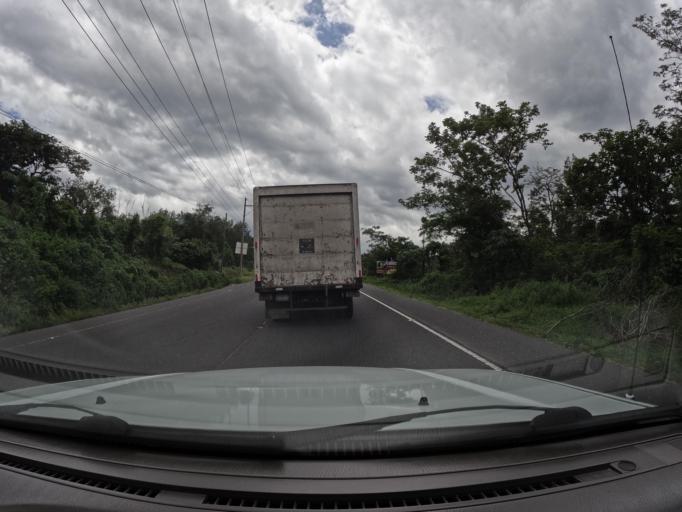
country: GT
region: Sacatepequez
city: Alotenango
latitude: 14.4707
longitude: -90.8127
